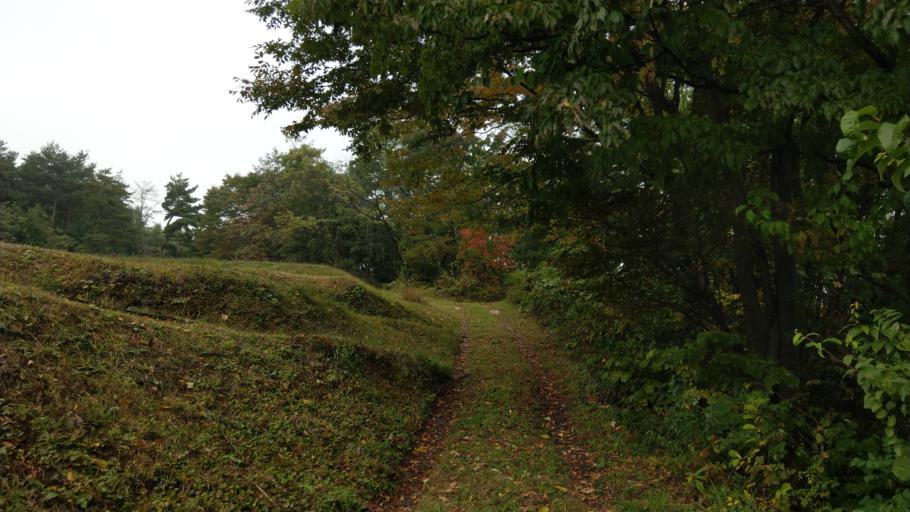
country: JP
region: Nagano
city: Komoro
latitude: 36.3557
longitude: 138.4170
